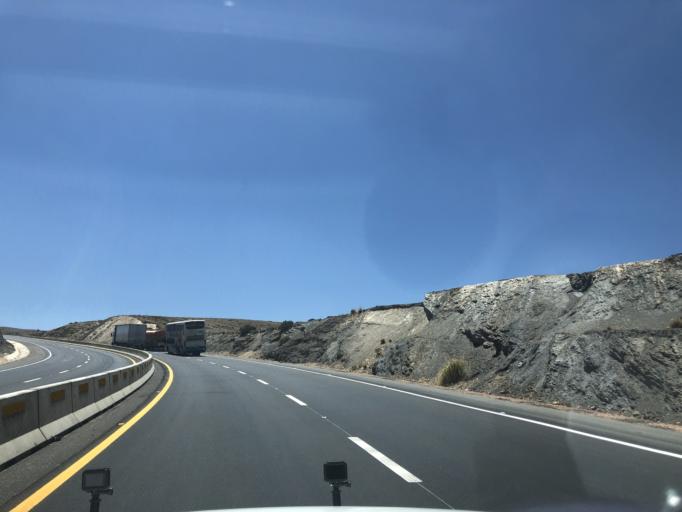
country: BO
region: Cochabamba
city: Colchani
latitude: -17.6893
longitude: -66.7535
